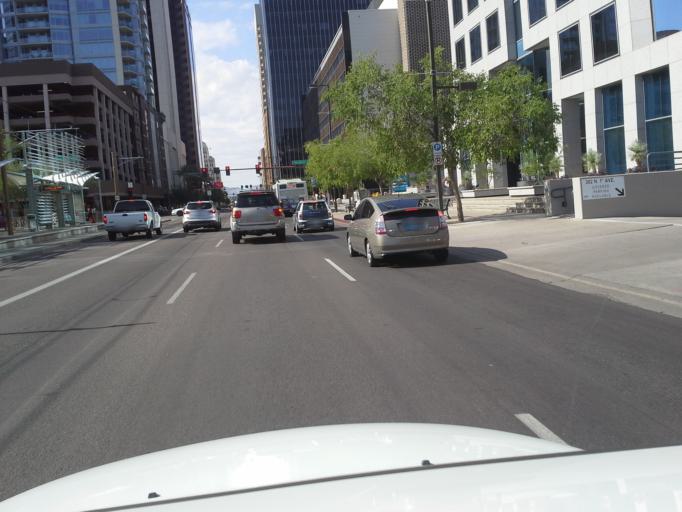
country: US
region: Arizona
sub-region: Maricopa County
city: Phoenix
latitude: 33.4522
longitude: -112.0752
